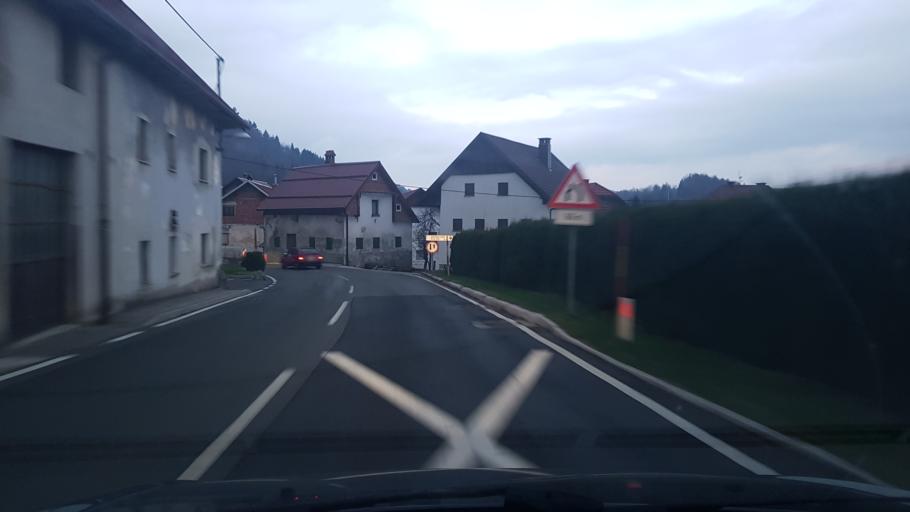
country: SI
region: Idrija
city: Idrija
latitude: 45.9242
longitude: 14.0439
